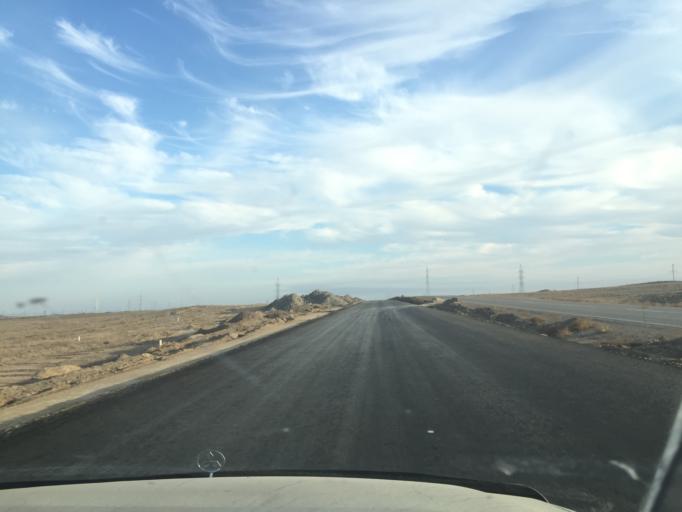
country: KZ
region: Almaty Oblysy
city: Ulken
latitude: 45.2163
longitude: 73.8675
